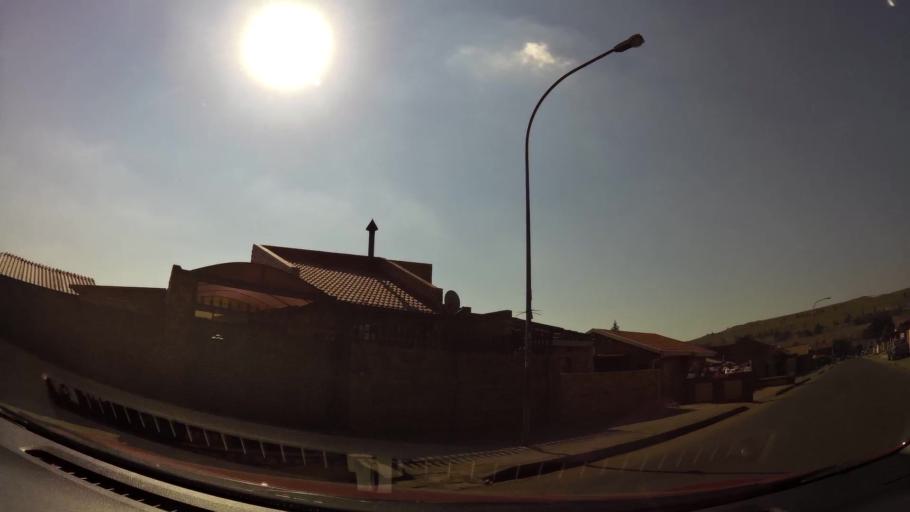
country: ZA
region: Gauteng
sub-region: City of Johannesburg Metropolitan Municipality
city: Johannesburg
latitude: -26.2410
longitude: 27.9560
